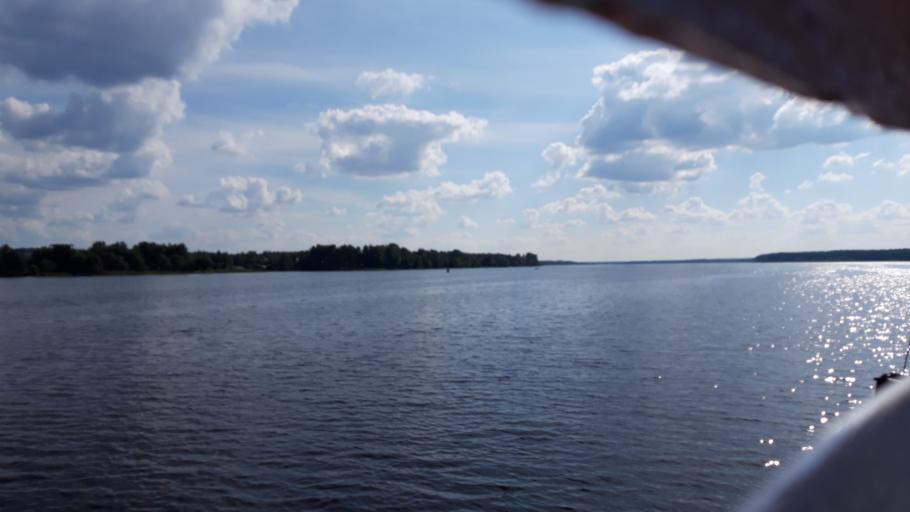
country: RU
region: Tverskaya
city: Konakovo
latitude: 56.6705
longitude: 36.6652
